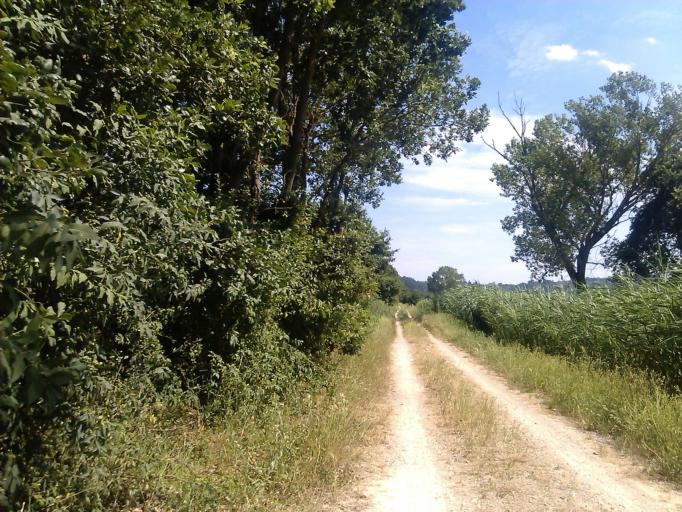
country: IT
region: Tuscany
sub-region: Provincia di Siena
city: Chiusi
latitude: 43.0599
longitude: 11.9340
